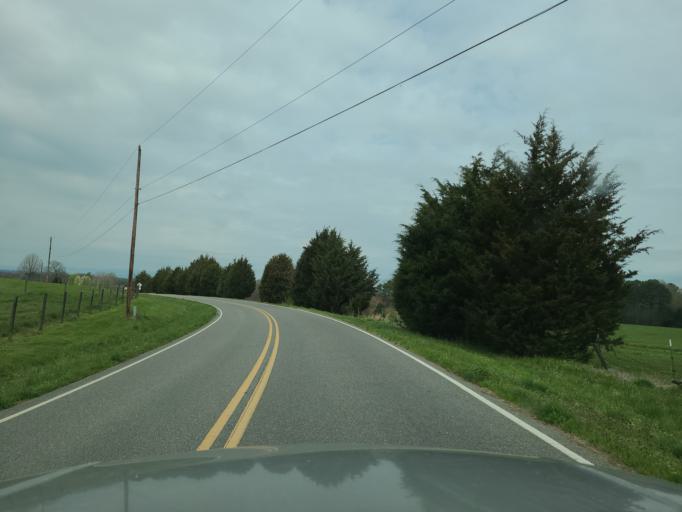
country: US
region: North Carolina
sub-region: Cleveland County
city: Shelby
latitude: 35.3196
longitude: -81.5235
